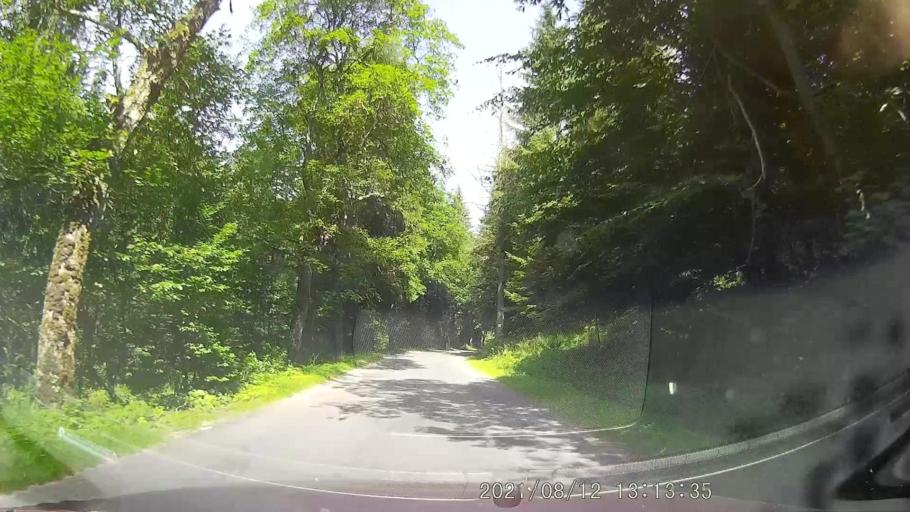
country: PL
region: Lower Silesian Voivodeship
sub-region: Powiat klodzki
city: Stronie Slaskie
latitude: 50.2545
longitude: 16.8543
